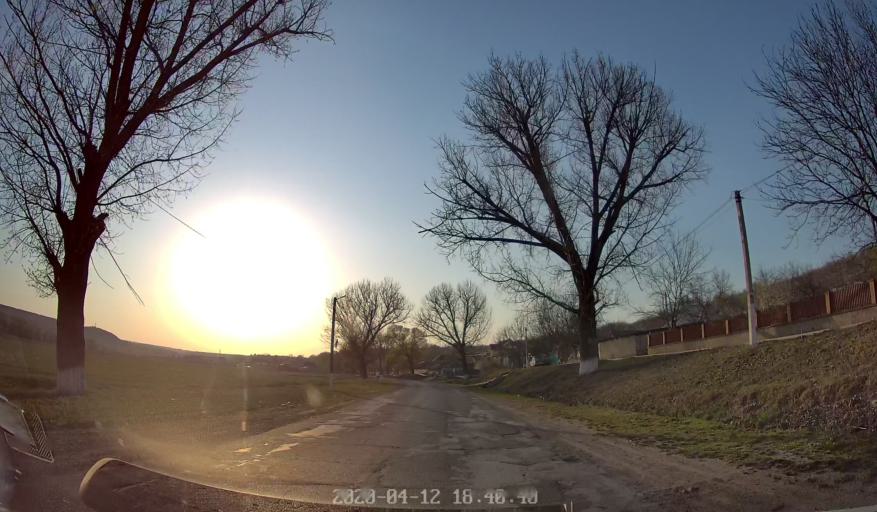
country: MD
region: Chisinau
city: Ciorescu
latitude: 47.1348
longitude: 28.9638
